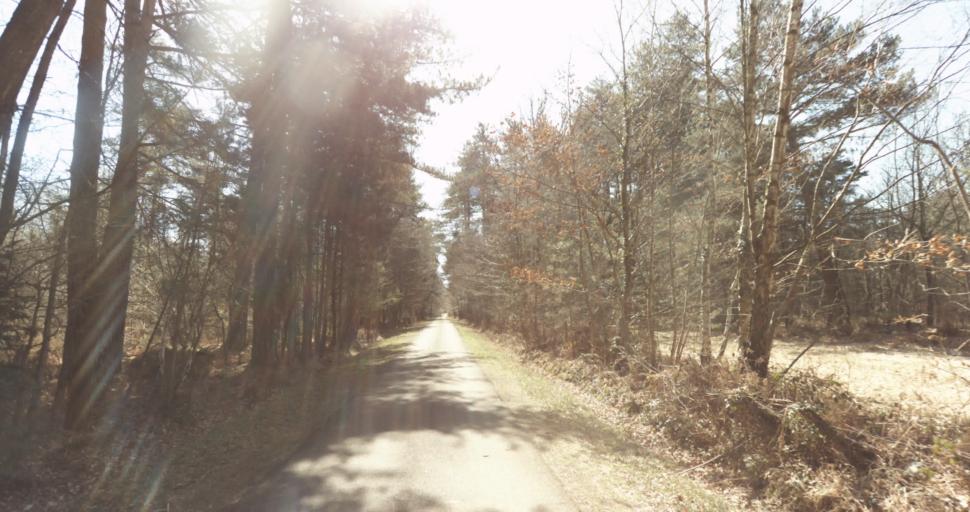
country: FR
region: Lower Normandy
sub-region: Departement du Calvados
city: Livarot
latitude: 49.0034
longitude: 0.0580
